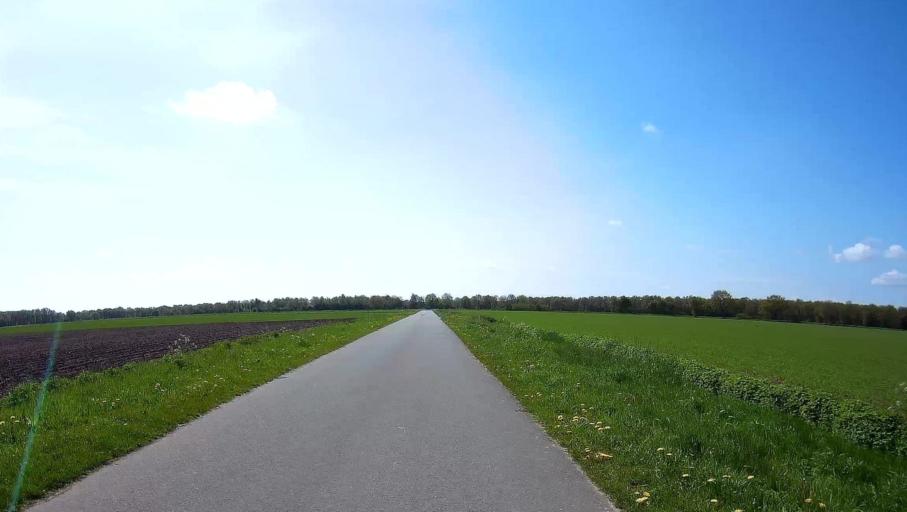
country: NL
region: Drenthe
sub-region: Gemeente Borger-Odoorn
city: Borger
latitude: 52.9865
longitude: 6.7916
